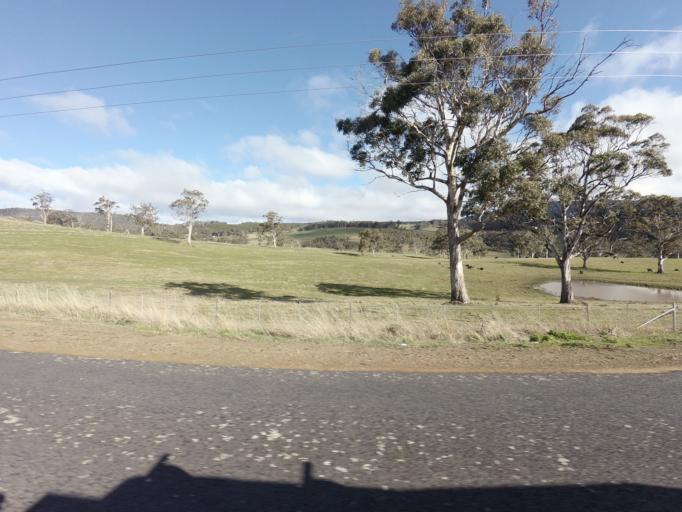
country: AU
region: Tasmania
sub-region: Derwent Valley
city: New Norfolk
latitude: -42.6312
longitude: 146.7341
